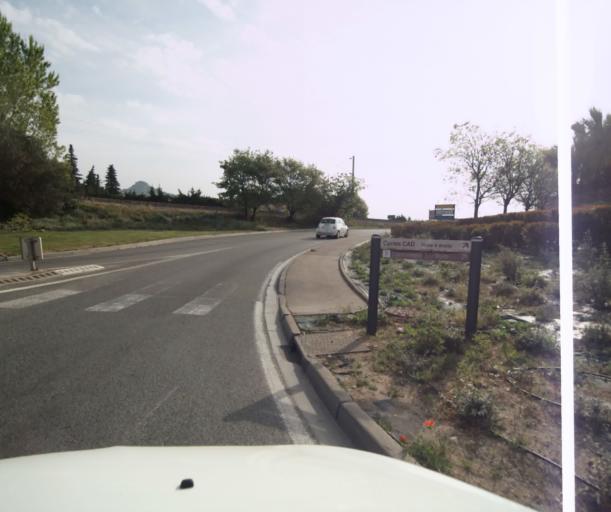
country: FR
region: Provence-Alpes-Cote d'Azur
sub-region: Departement du Var
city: Hyeres
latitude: 43.1136
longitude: 6.1095
